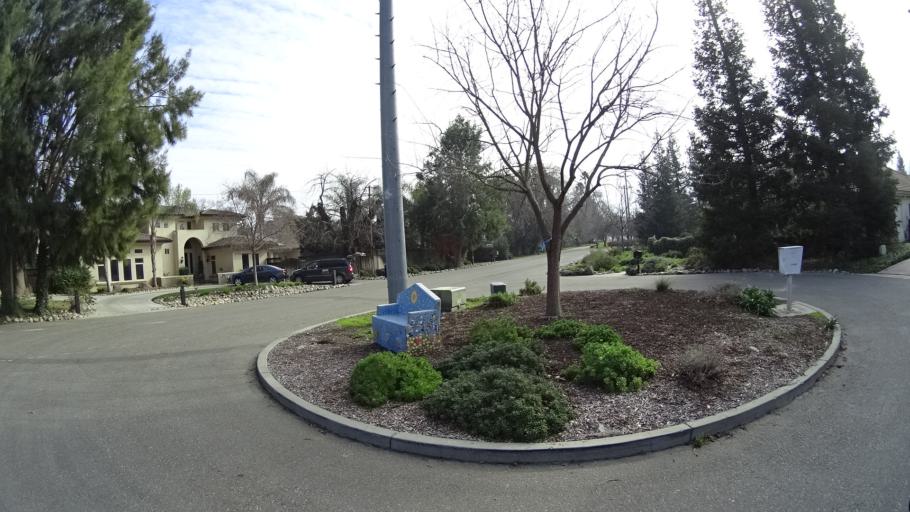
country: US
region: California
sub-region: Yolo County
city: Davis
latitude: 38.5411
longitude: -121.7136
